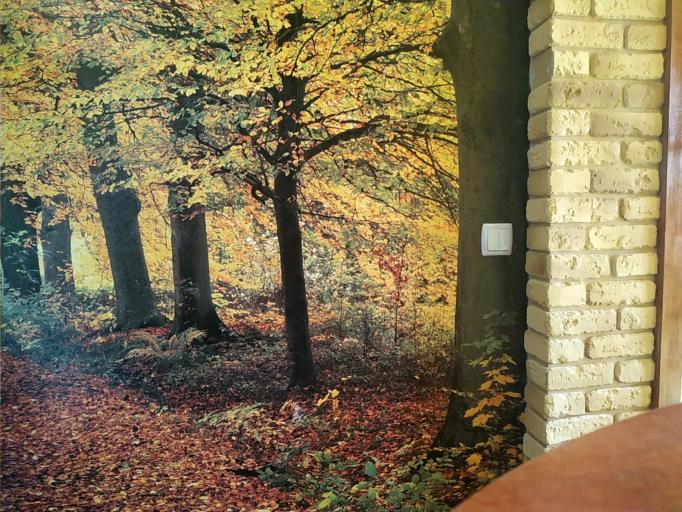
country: RU
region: Jaroslavl
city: Kukoboy
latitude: 58.8999
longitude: 39.6943
